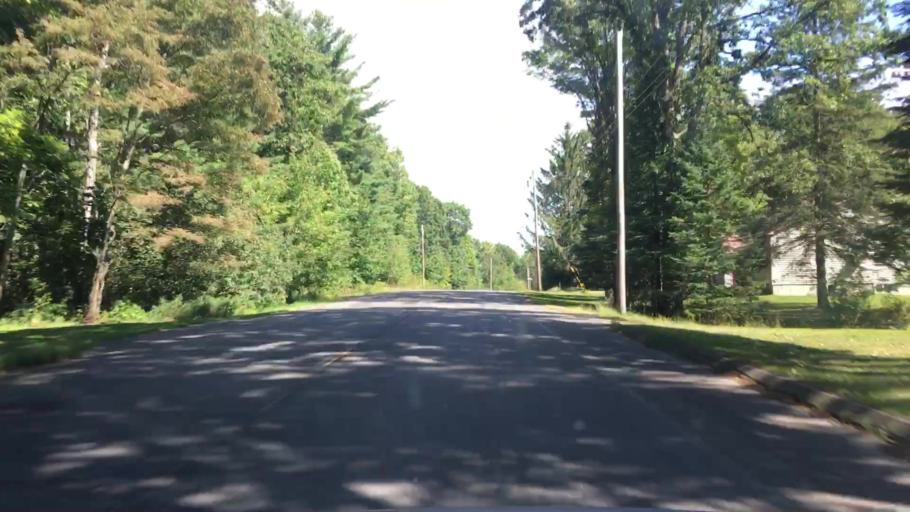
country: US
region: Maine
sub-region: Penobscot County
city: Garland
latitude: 45.0852
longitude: -69.2265
